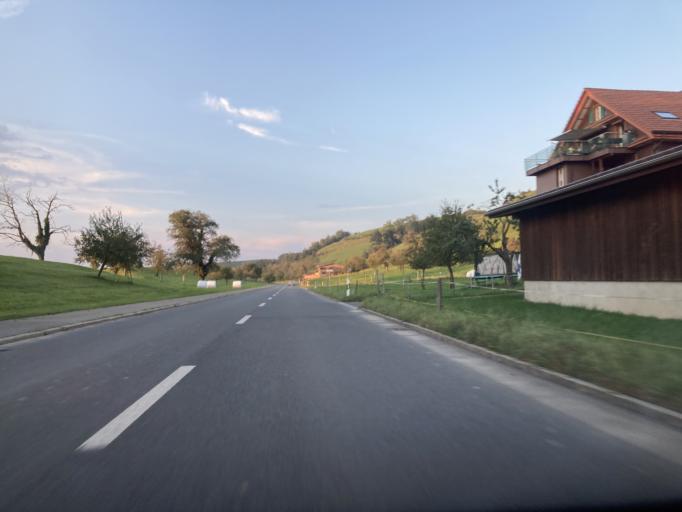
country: CH
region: Zug
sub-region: Zug
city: Menzingen
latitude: 47.1663
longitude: 8.5666
